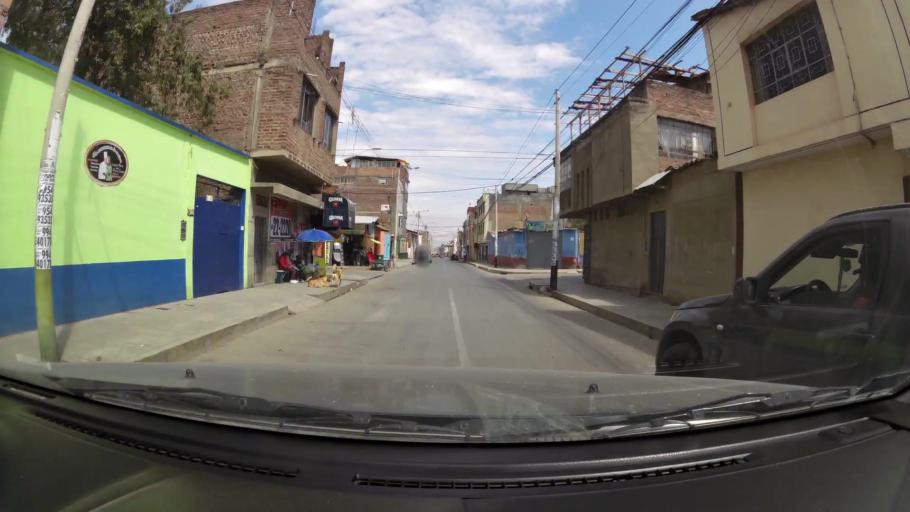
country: PE
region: Junin
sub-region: Provincia de Huancayo
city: El Tambo
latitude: -12.0732
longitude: -75.2149
